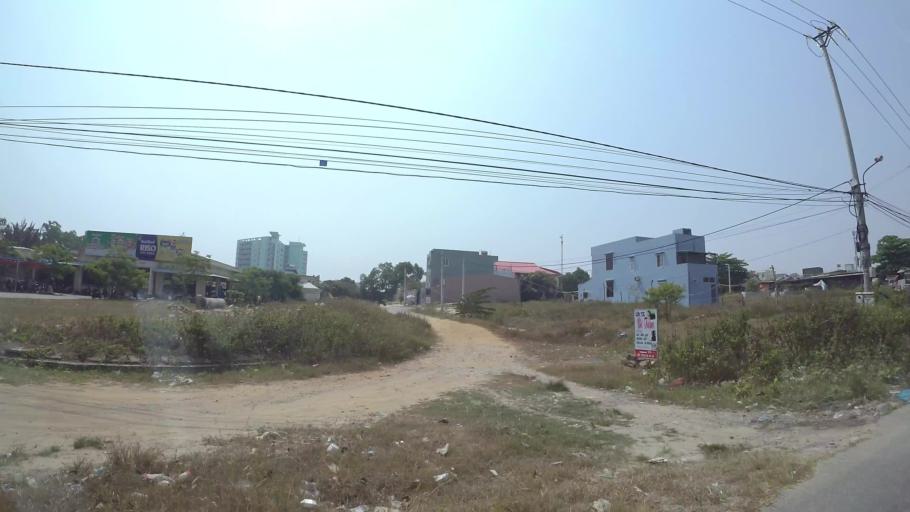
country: VN
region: Da Nang
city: Ngu Hanh Son
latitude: 16.0254
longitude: 108.2476
